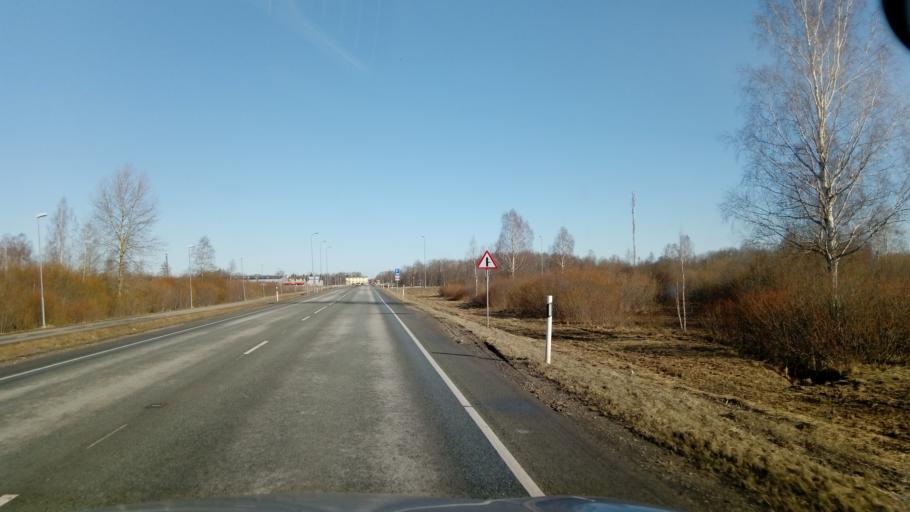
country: EE
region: Laeaene-Virumaa
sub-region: Rakvere linn
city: Rakvere
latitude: 59.3442
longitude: 26.3414
